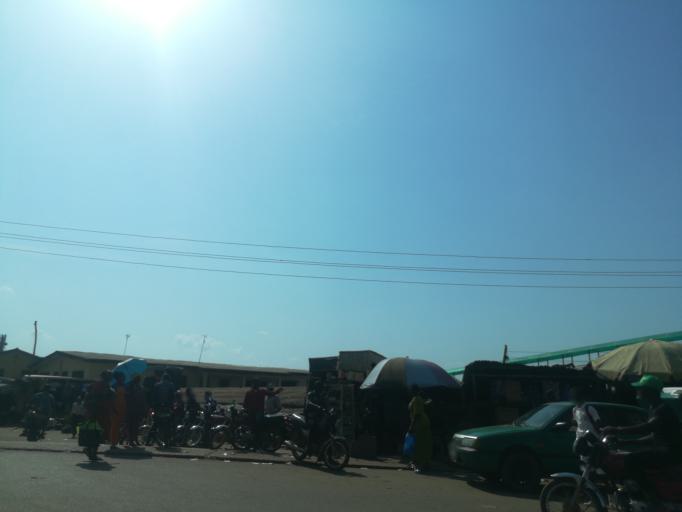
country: NG
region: Ogun
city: Abeokuta
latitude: 7.1344
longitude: 3.3314
